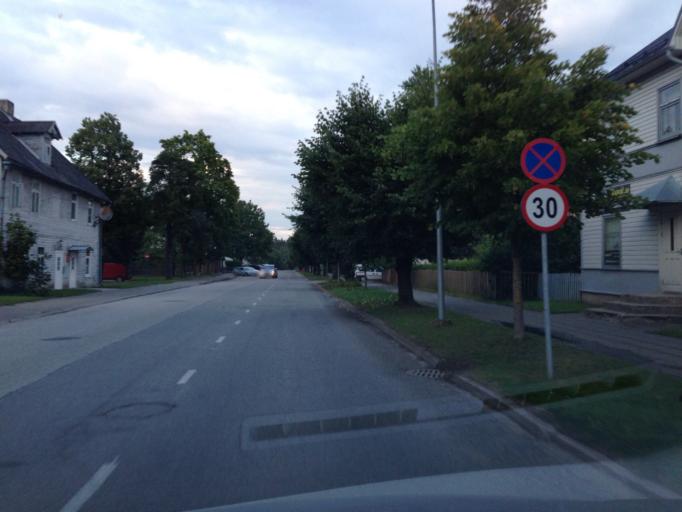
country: EE
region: Tartu
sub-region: Elva linn
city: Elva
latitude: 58.2216
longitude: 26.4090
